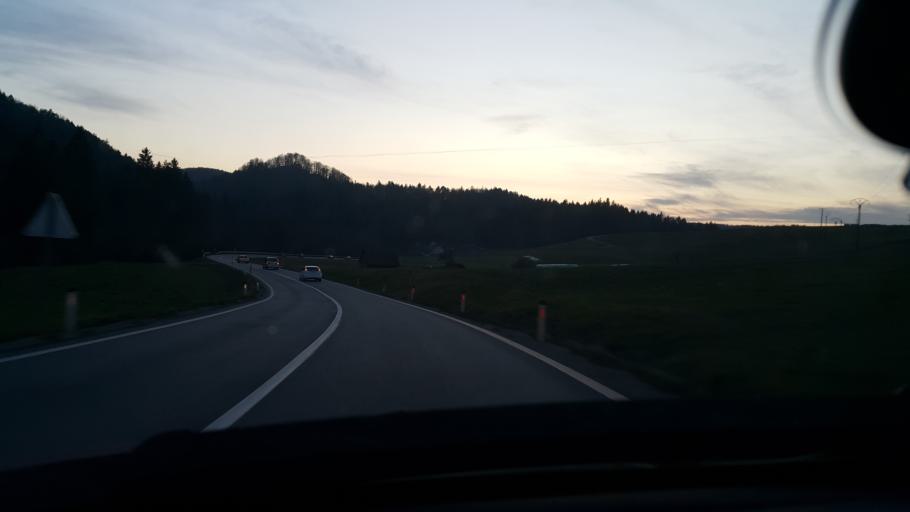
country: SI
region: Dobrna
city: Dobrna
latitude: 46.3215
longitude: 15.1810
